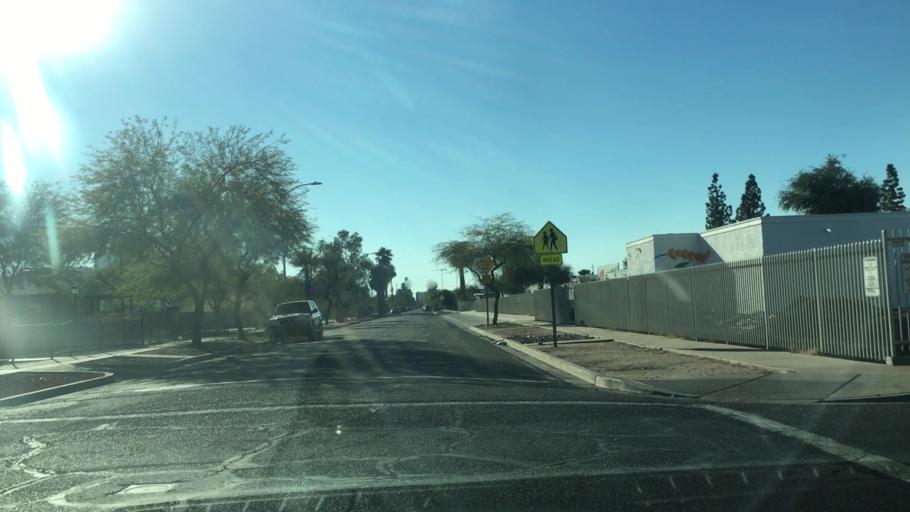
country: US
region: Arizona
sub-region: Maricopa County
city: Phoenix
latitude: 33.4568
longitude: -112.0521
